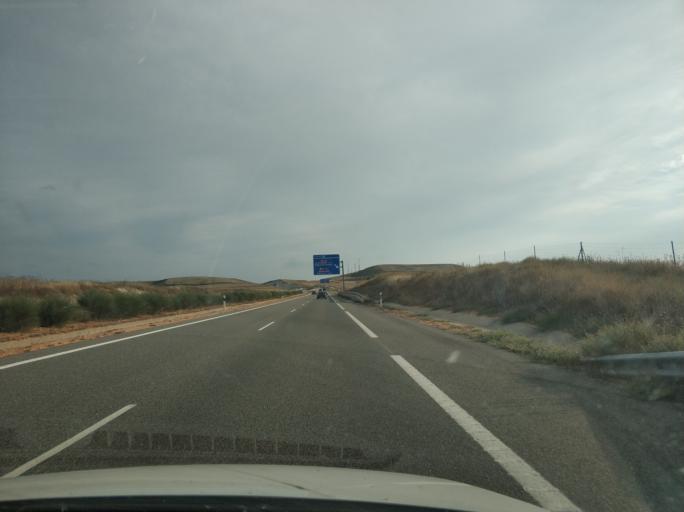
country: ES
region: Castille and Leon
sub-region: Provincia de Burgos
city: Sotragero
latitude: 42.4037
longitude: -3.6982
